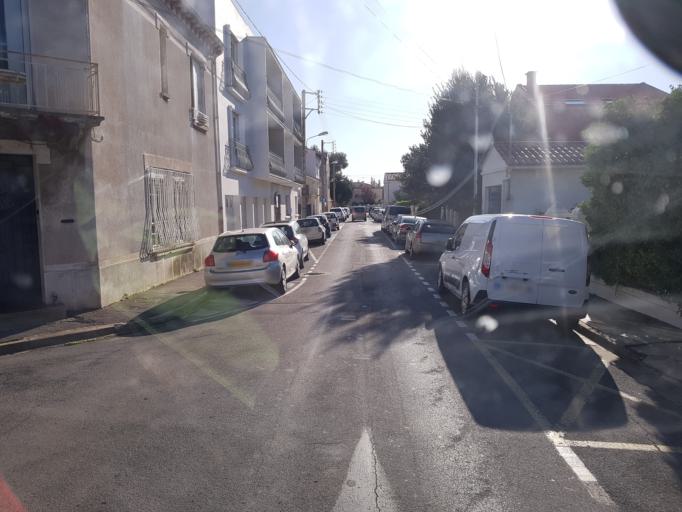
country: FR
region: Languedoc-Roussillon
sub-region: Departement de l'Aude
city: Narbonne
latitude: 43.1792
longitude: 3.0062
